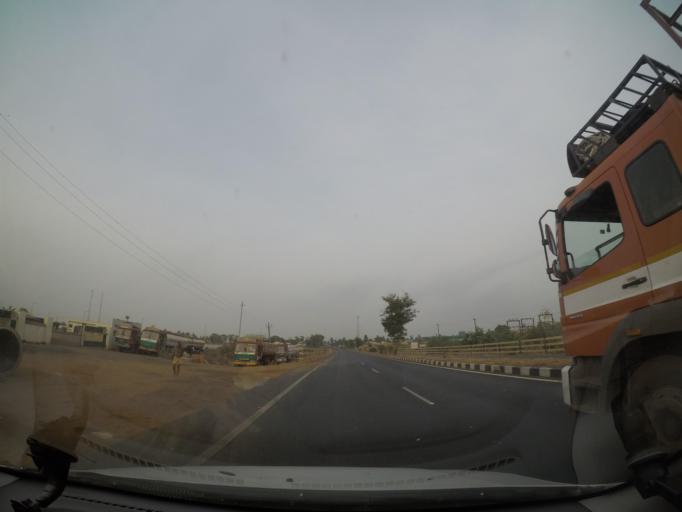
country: IN
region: Andhra Pradesh
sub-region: Krishna
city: Gannavaram
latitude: 16.6004
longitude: 80.8967
